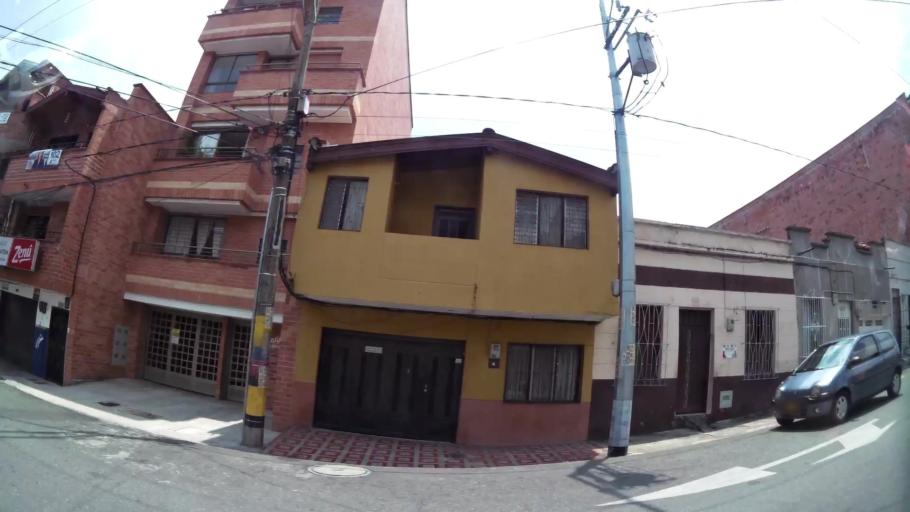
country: CO
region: Antioquia
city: Medellin
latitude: 6.2467
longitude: -75.6110
